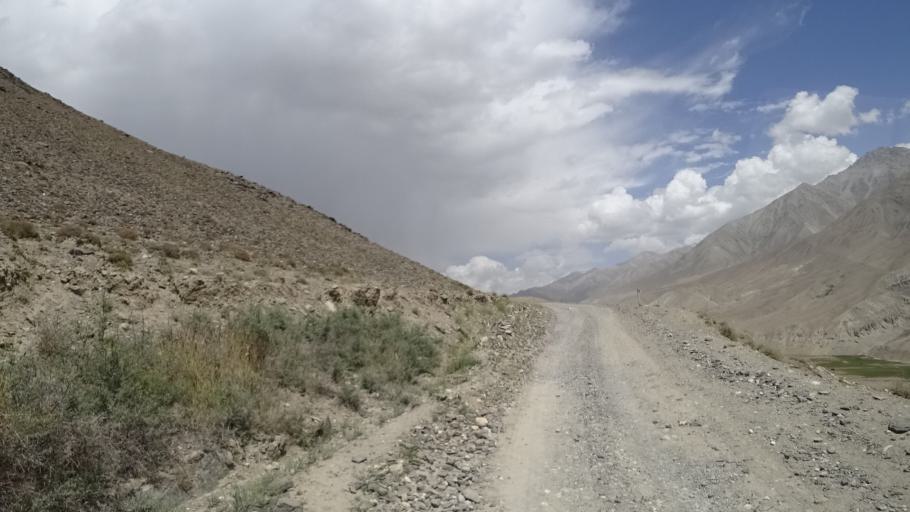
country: AF
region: Badakhshan
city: Khandud
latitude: 37.0877
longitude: 72.7028
